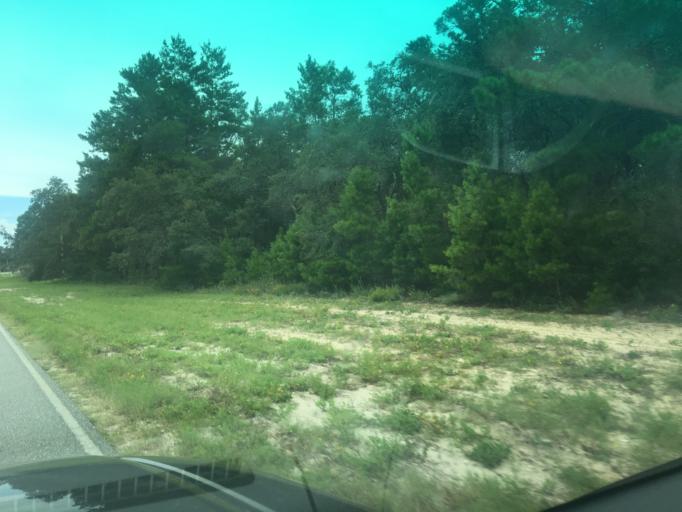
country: US
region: Florida
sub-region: Wakulla County
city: Crawfordville
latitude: 29.9036
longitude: -84.3512
